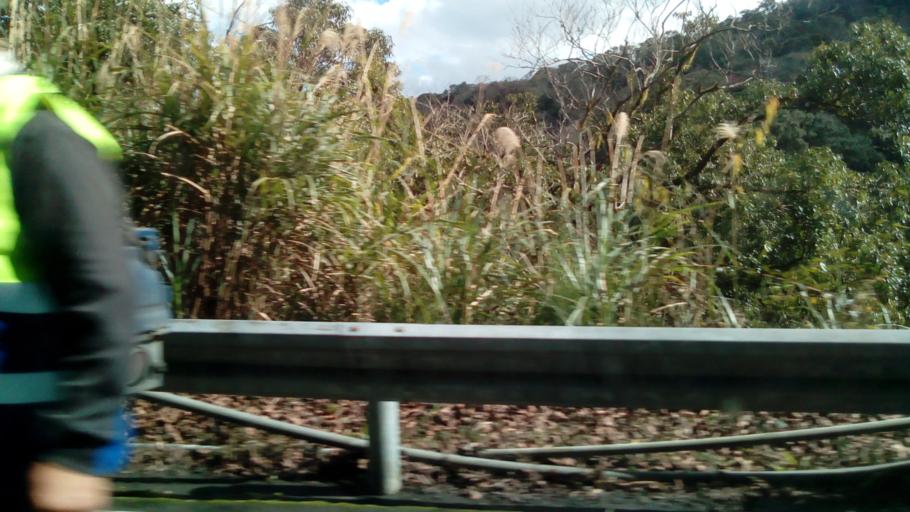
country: TW
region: Taiwan
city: Daxi
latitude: 24.4047
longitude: 121.3603
